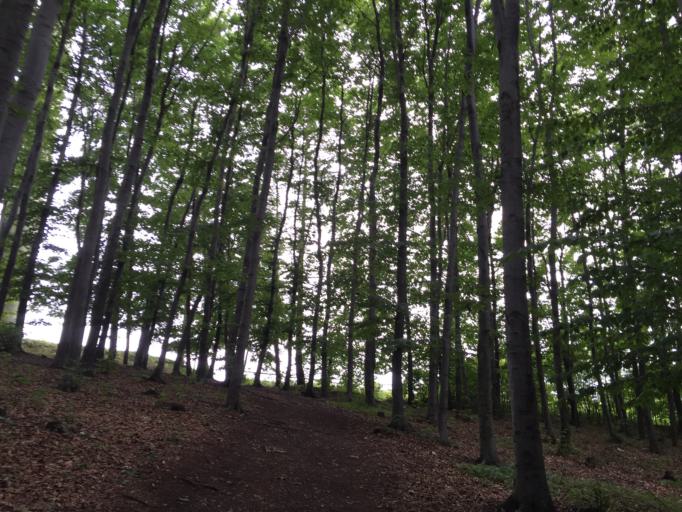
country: PL
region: Lesser Poland Voivodeship
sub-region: Powiat olkuski
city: Klucze
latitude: 50.3369
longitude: 19.5495
